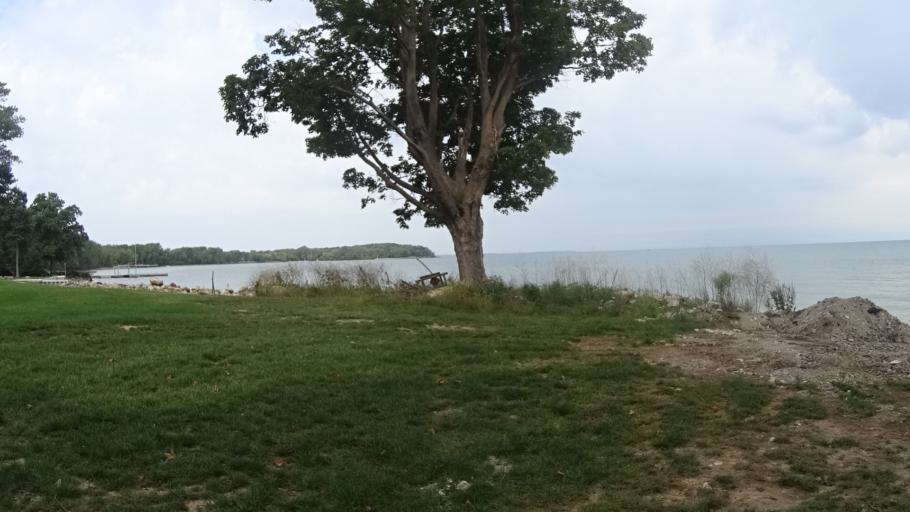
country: US
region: Ohio
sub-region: Erie County
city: Sandusky
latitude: 41.6108
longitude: -82.6922
